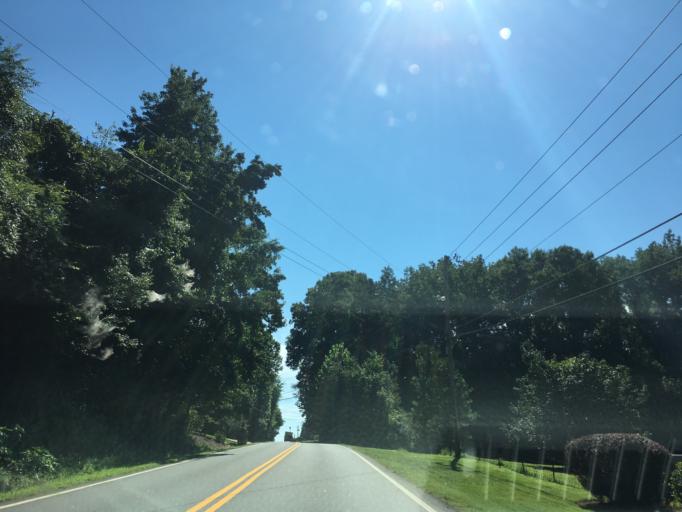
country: US
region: Georgia
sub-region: Fulton County
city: Milton
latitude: 34.1630
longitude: -84.3092
